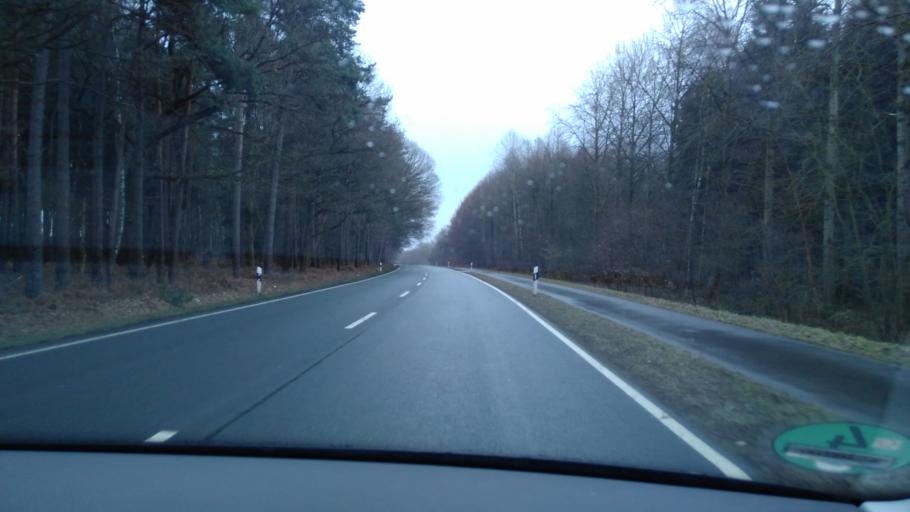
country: DE
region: North Rhine-Westphalia
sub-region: Regierungsbezirk Detmold
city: Oerlinghausen
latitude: 51.9144
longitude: 8.6405
